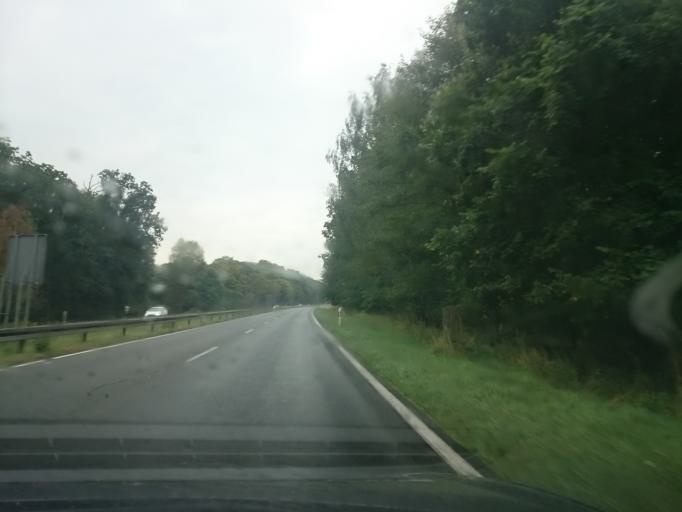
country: DE
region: Brandenburg
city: Oranienburg
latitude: 52.8265
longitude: 13.2083
